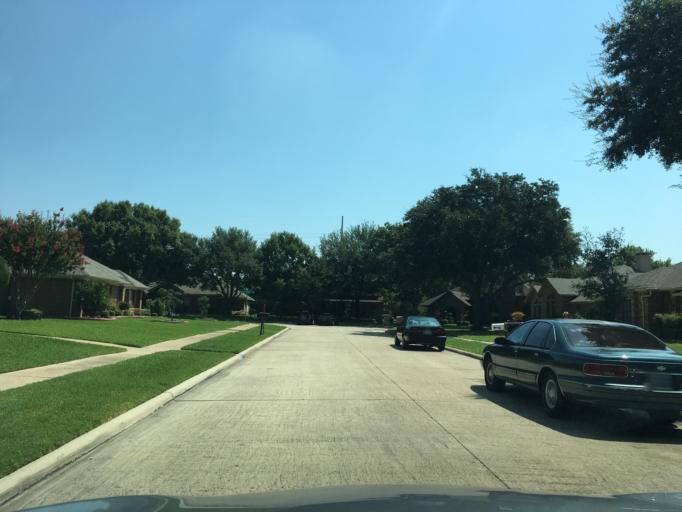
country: US
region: Texas
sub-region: Dallas County
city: Garland
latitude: 32.9395
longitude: -96.6670
